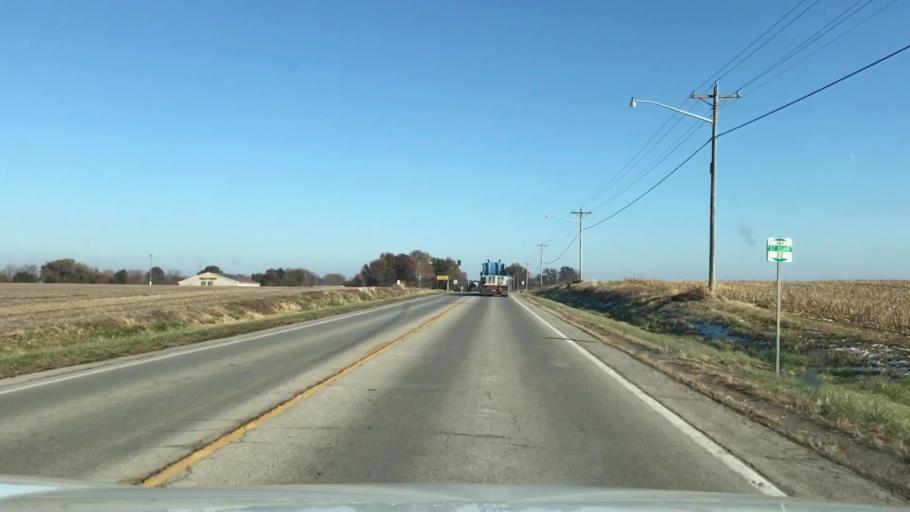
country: US
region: Illinois
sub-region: Clinton County
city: New Baden
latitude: 38.5353
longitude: -89.7184
